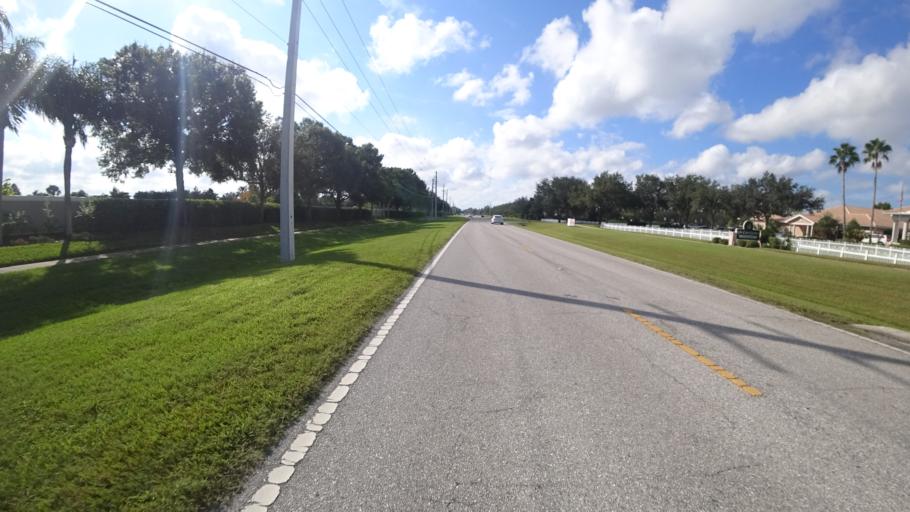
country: US
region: Florida
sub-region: Sarasota County
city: North Sarasota
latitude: 27.3950
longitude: -82.5136
